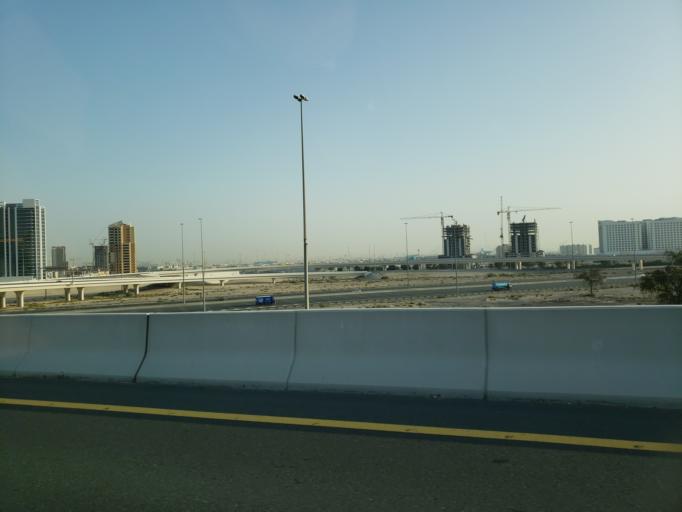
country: AE
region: Dubai
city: Dubai
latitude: 25.0497
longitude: 55.2233
